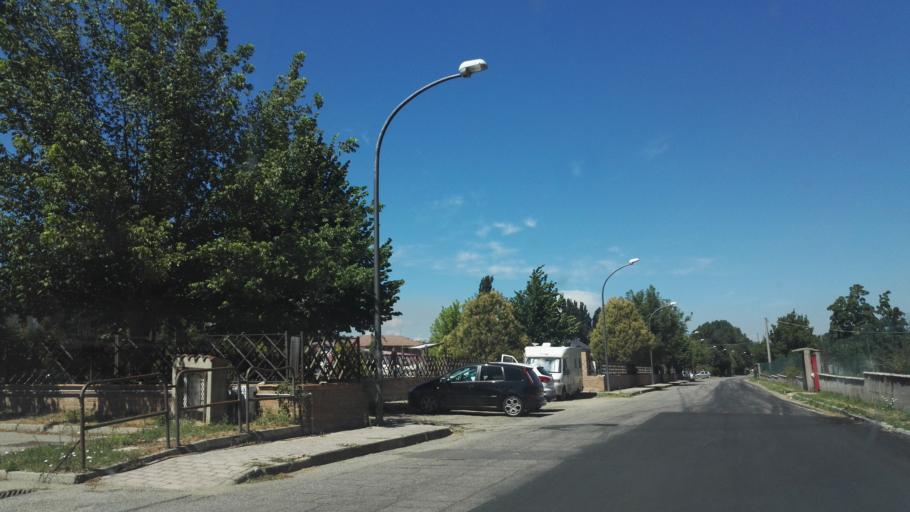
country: IT
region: Calabria
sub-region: Provincia di Vibo-Valentia
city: Serra San Bruno
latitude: 38.5722
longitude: 16.3301
